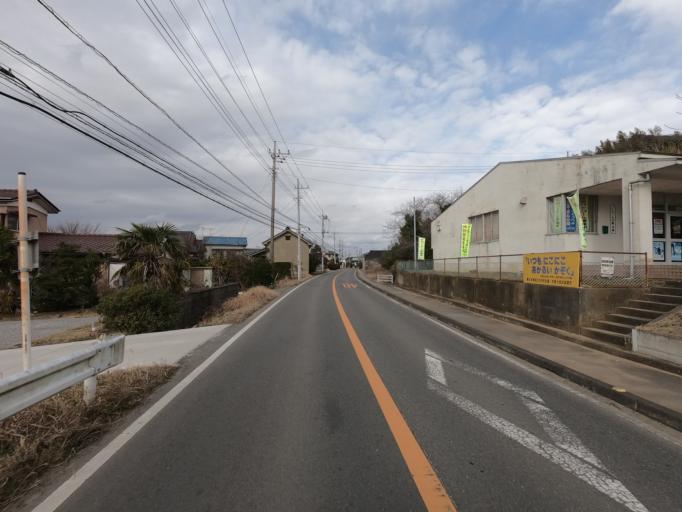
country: JP
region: Ibaraki
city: Inashiki
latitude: 36.0846
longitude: 140.4240
